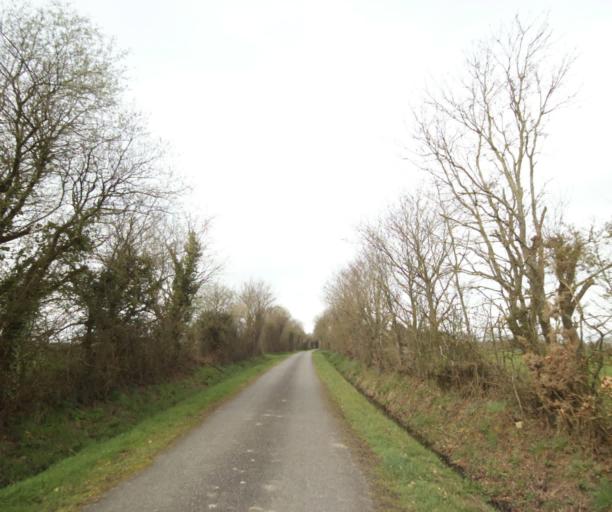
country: FR
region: Pays de la Loire
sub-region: Departement de la Loire-Atlantique
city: Bouvron
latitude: 47.4213
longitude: -1.8862
